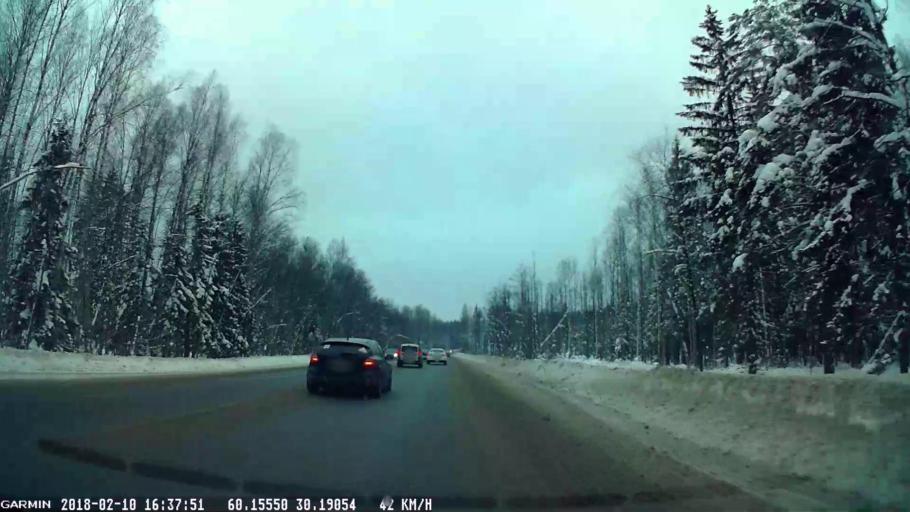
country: RU
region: Leningrad
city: Sertolovo
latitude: 60.1518
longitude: 30.1952
